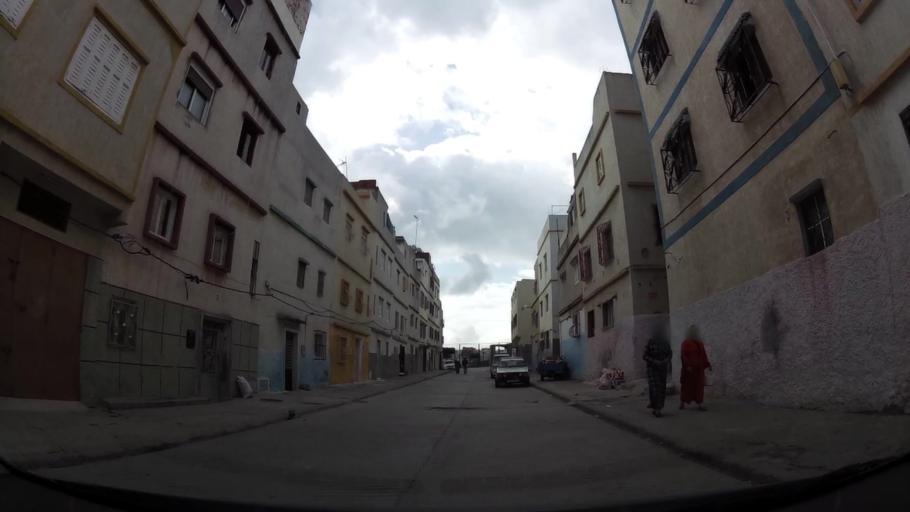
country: MA
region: Tanger-Tetouan
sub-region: Tanger-Assilah
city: Tangier
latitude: 35.7609
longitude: -5.8245
